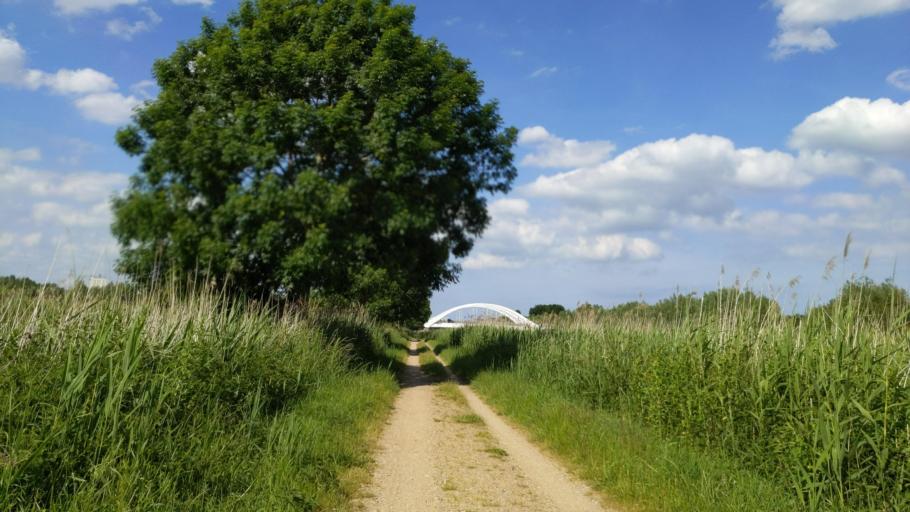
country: DE
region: Schleswig-Holstein
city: Krummesse
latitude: 53.8284
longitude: 10.6377
